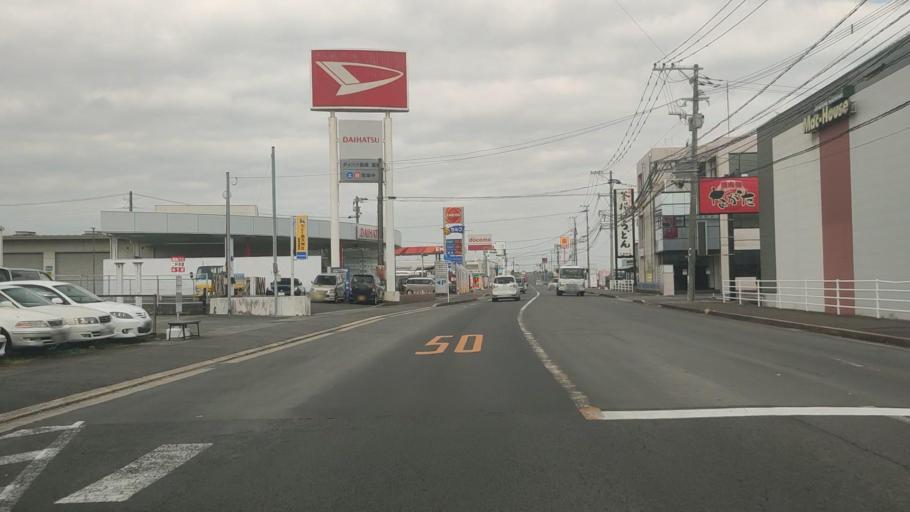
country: JP
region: Nagasaki
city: Shimabara
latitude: 32.8044
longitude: 130.3626
